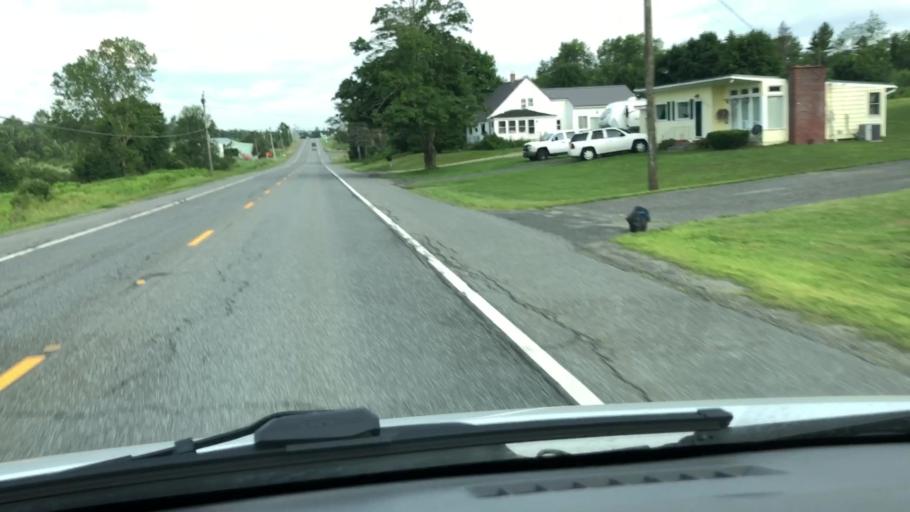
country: US
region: Massachusetts
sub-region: Berkshire County
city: Hinsdale
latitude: 42.5097
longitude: -73.0492
